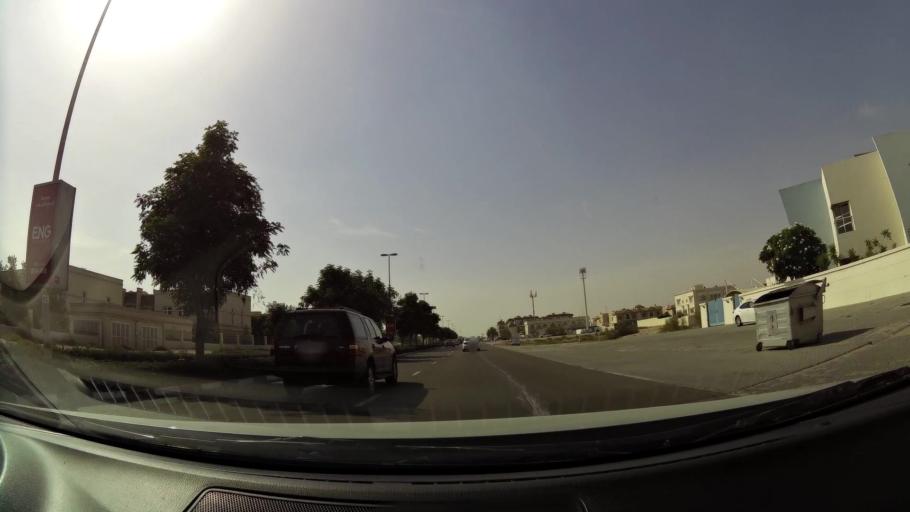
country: AE
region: Ash Shariqah
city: Sharjah
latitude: 25.2204
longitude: 55.4235
